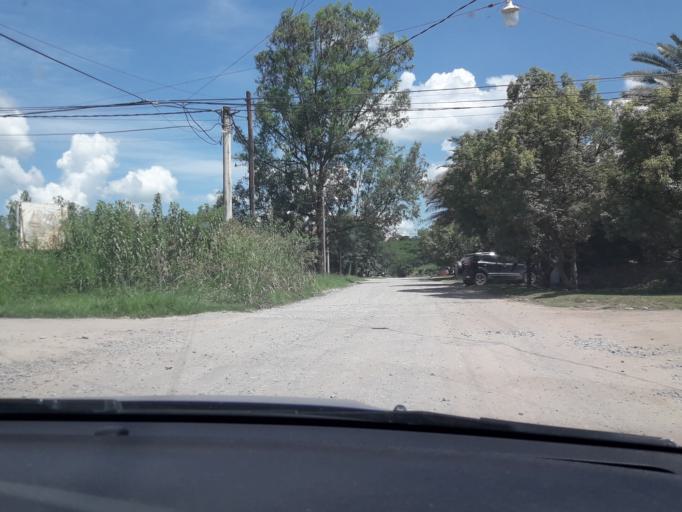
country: AR
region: Jujuy
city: San Salvador de Jujuy
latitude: -24.1814
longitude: -65.3361
